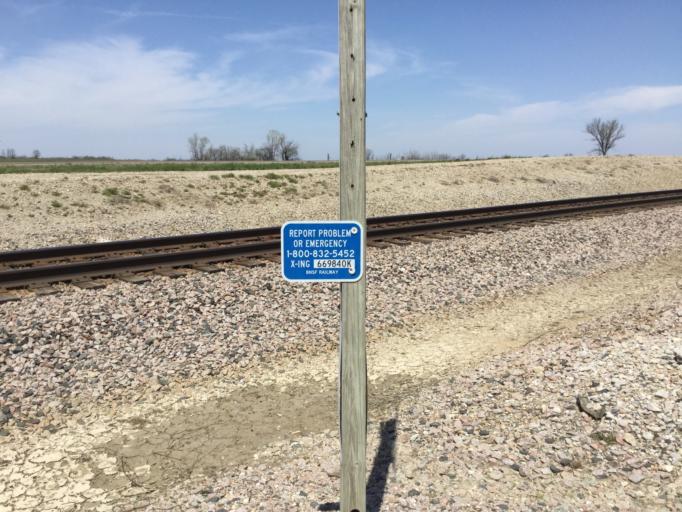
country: US
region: Kansas
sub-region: Bourbon County
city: Fort Scott
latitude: 37.7325
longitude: -94.7550
